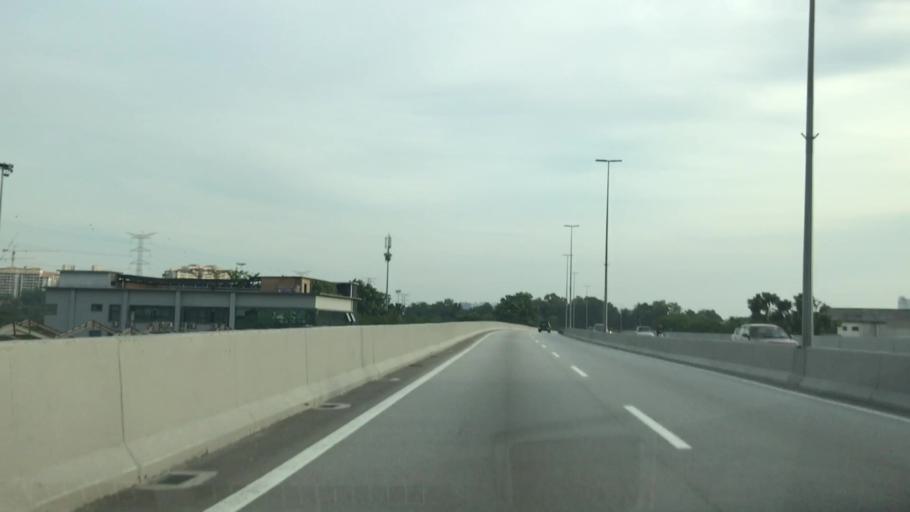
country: MY
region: Kuala Lumpur
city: Kuala Lumpur
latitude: 3.1130
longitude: 101.7124
